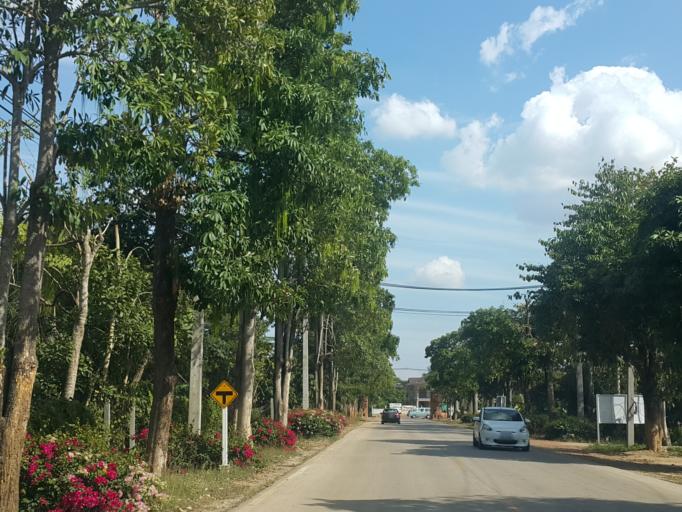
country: TH
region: Sukhothai
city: Si Samrong
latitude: 17.2282
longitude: 99.8457
